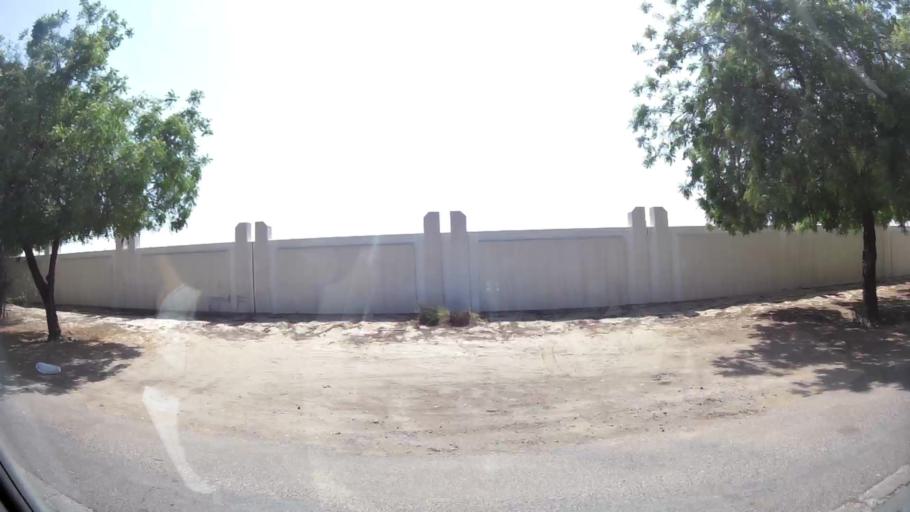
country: AE
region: Ash Shariqah
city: Sharjah
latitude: 25.2707
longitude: 55.3599
